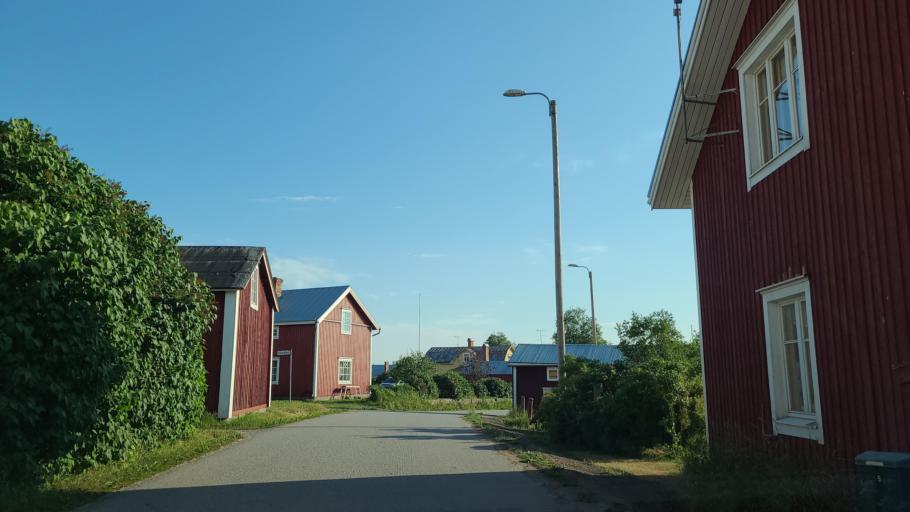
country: FI
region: Ostrobothnia
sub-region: Vaasa
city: Replot
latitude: 63.3464
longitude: 21.3369
